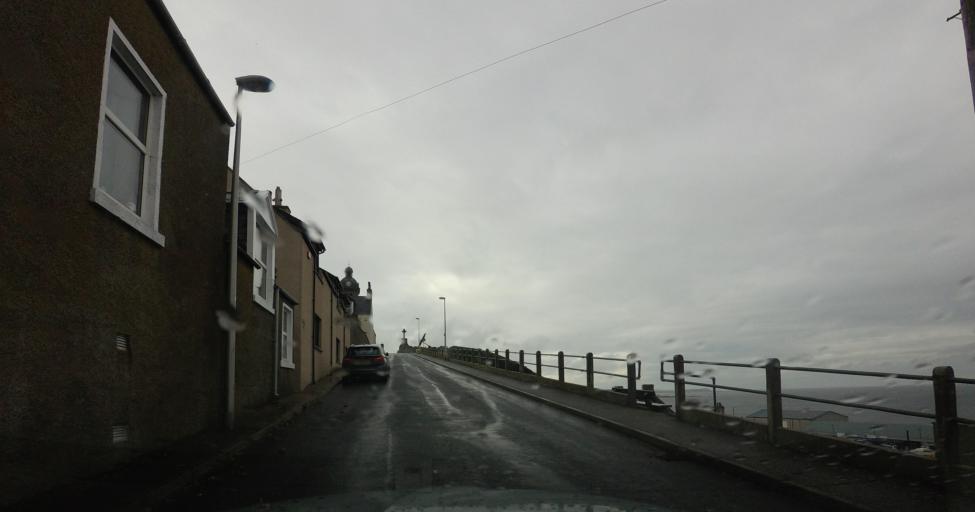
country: GB
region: Scotland
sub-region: Aberdeenshire
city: Macduff
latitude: 57.6687
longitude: -2.5005
